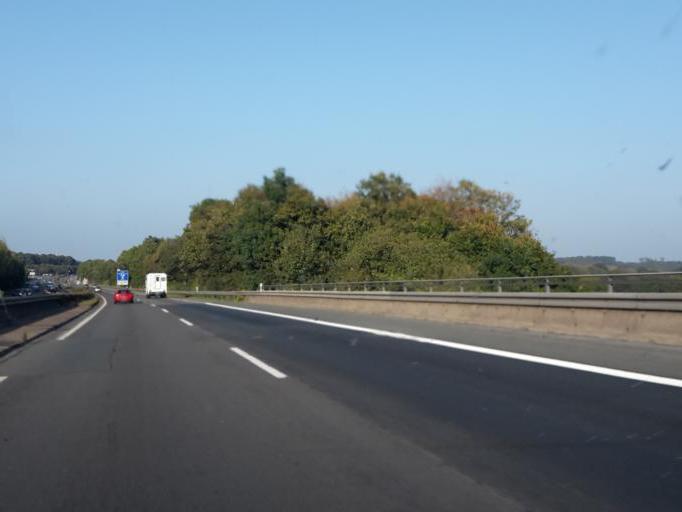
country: DE
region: North Rhine-Westphalia
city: Lengerich
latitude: 52.2232
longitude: 7.8728
